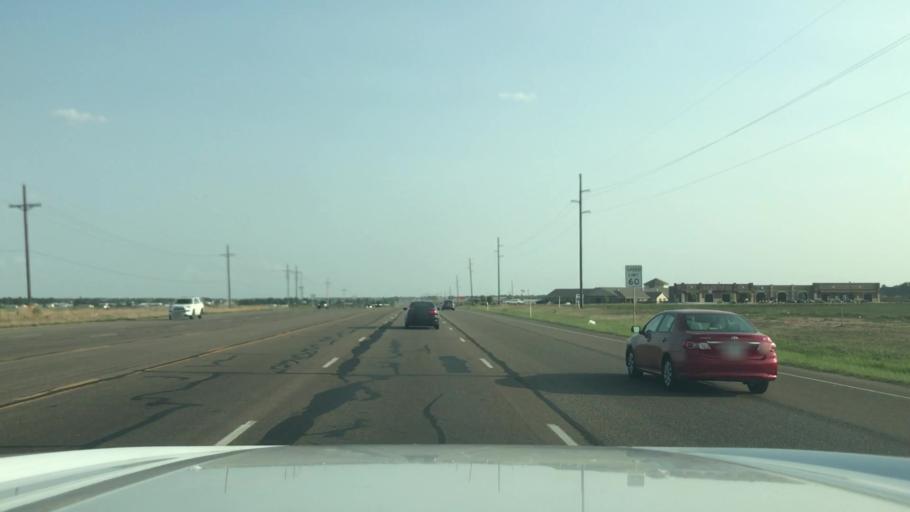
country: US
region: Texas
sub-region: Potter County
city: Amarillo
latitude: 35.1431
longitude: -101.9382
